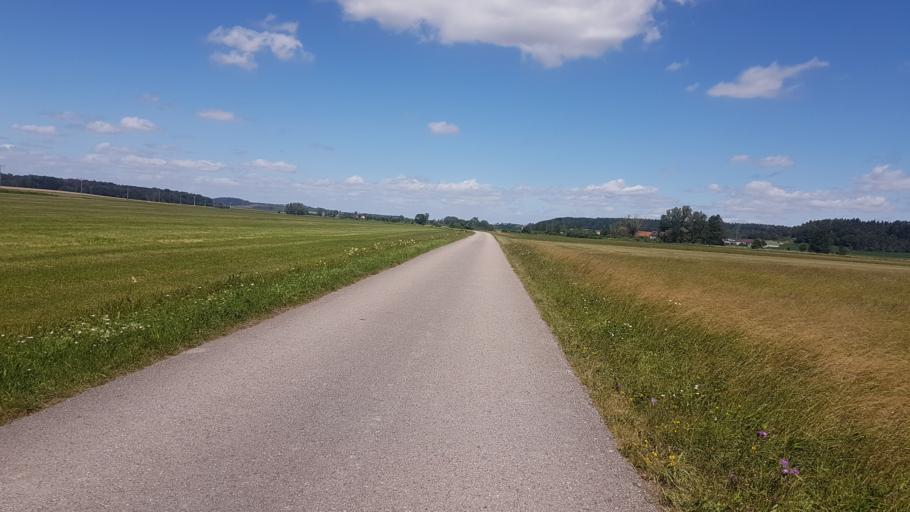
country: DE
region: Bavaria
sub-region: Regierungsbezirk Mittelfranken
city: Aurach
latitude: 49.2685
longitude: 10.4434
